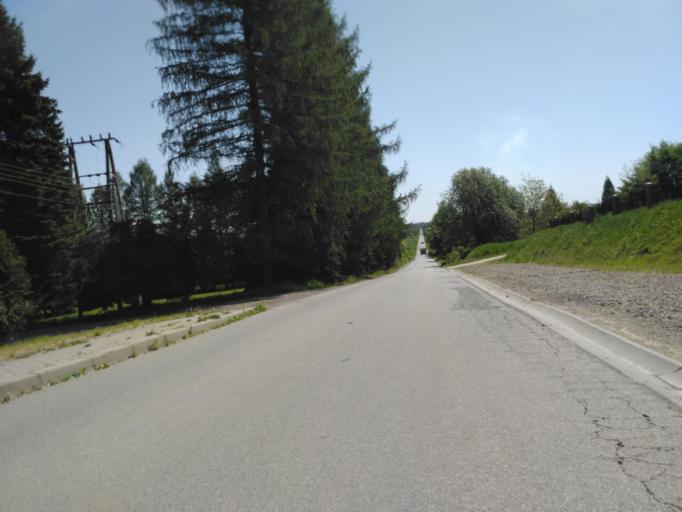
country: PL
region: Subcarpathian Voivodeship
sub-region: Powiat krosnienski
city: Miejsce Piastowe
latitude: 49.6115
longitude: 21.7591
